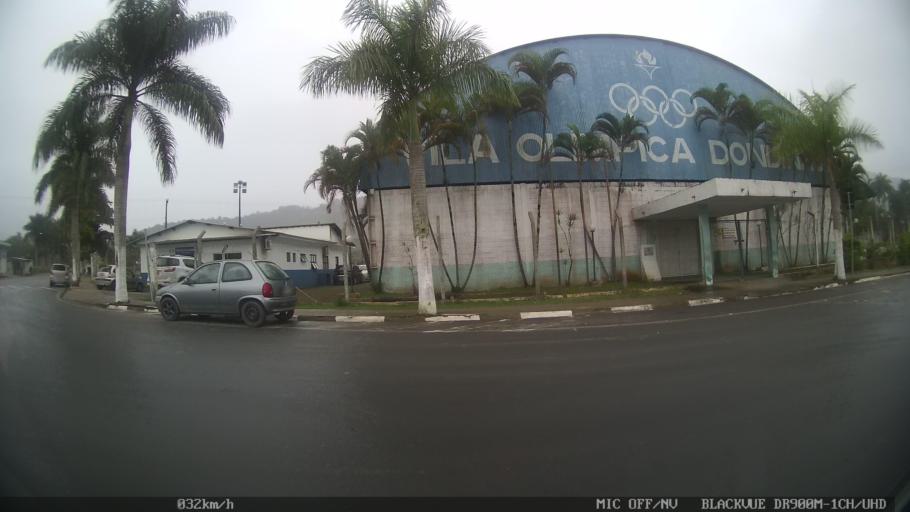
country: BR
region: Sao Paulo
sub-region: Juquia
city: Juquia
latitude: -24.3187
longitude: -47.6406
